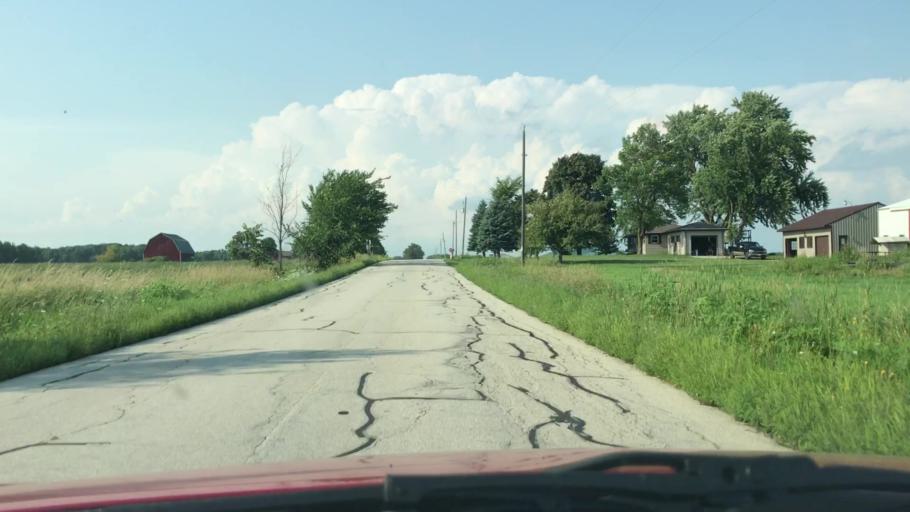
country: US
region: Wisconsin
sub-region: Brown County
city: Oneida
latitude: 44.4427
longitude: -88.1704
